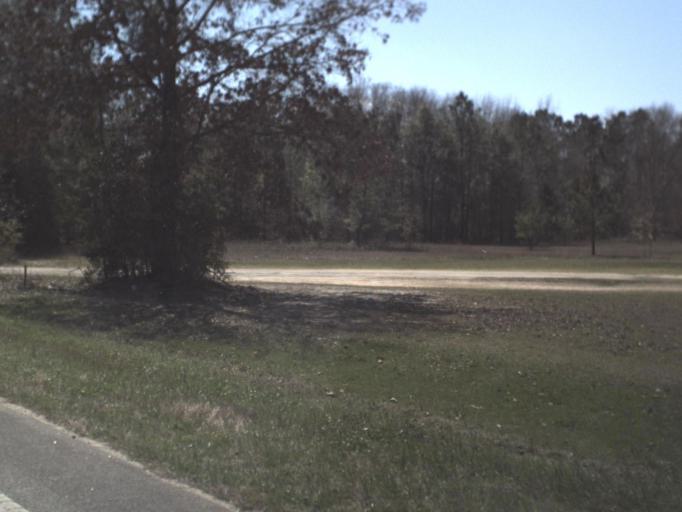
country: US
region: Florida
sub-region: Gadsden County
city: Gretna
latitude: 30.6879
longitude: -84.6214
